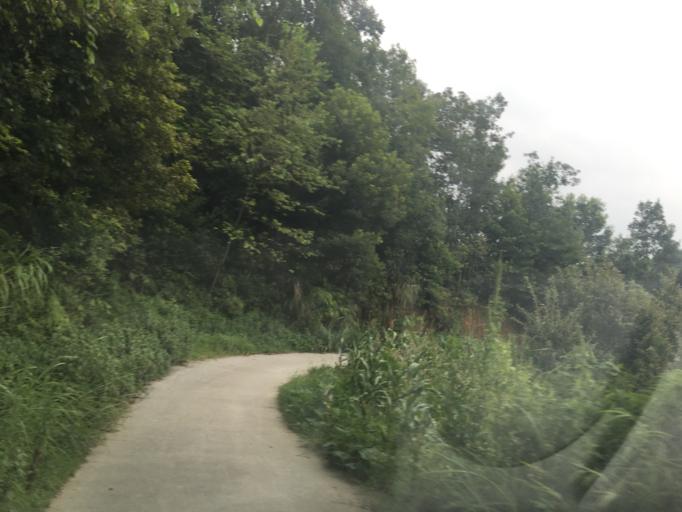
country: CN
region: Guangxi Zhuangzu Zizhiqu
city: Xinzhou
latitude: 25.1571
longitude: 105.6980
